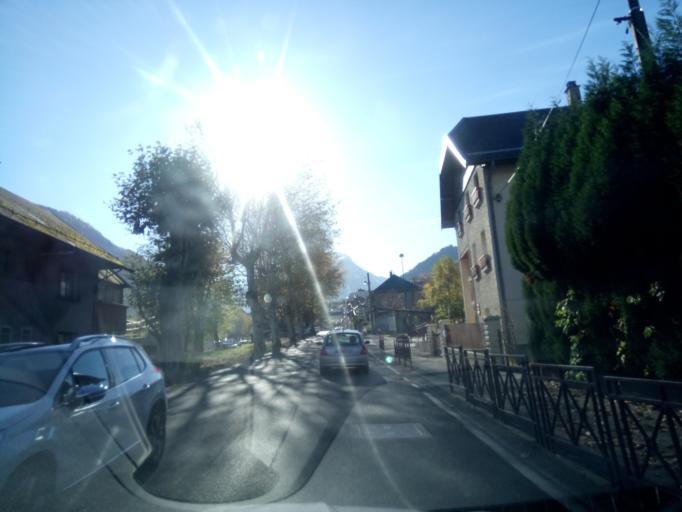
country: FR
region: Rhone-Alpes
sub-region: Departement de la Savoie
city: Saint-Jean-de-Maurienne
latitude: 45.2814
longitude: 6.3473
